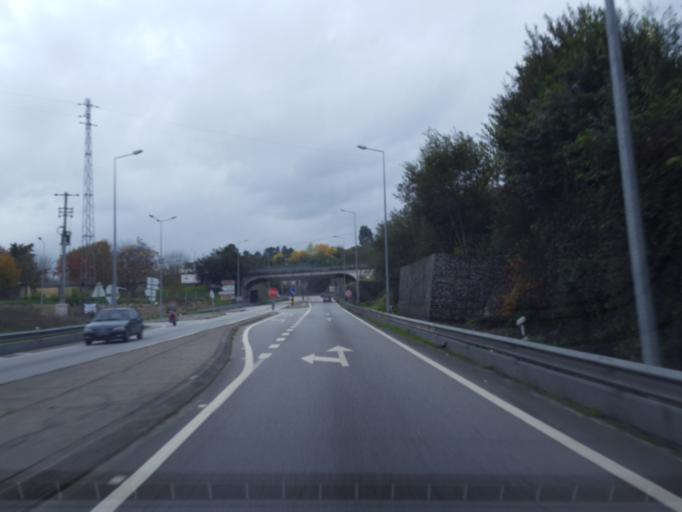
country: PT
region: Porto
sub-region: Marco de Canaveses
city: Marco de Canavezes
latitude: 41.1988
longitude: -8.1613
